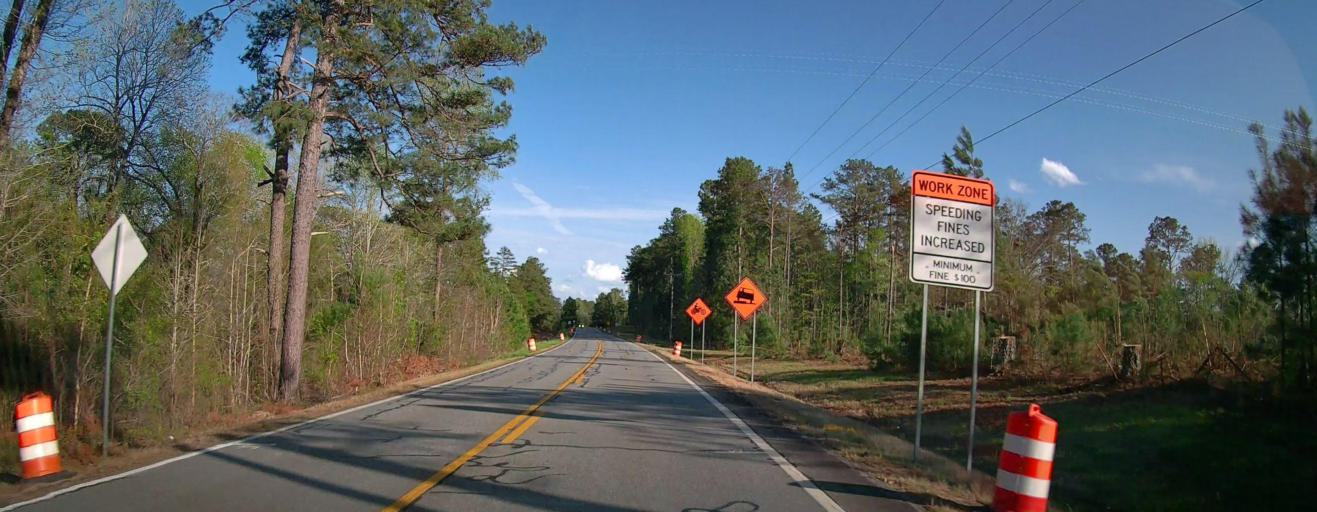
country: US
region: Georgia
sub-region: Baldwin County
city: Milledgeville
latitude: 33.1252
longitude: -83.2971
